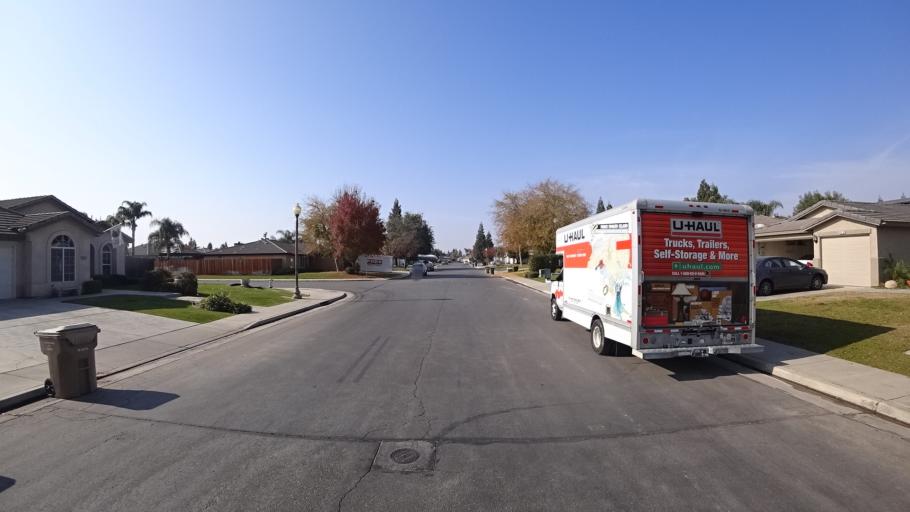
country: US
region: California
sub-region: Kern County
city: Greenacres
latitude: 35.4247
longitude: -119.1124
